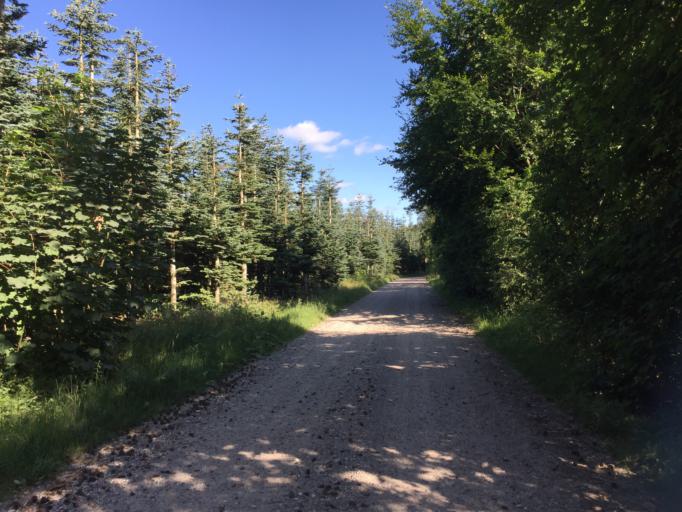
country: DK
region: South Denmark
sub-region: Kerteminde Kommune
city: Langeskov
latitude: 55.3609
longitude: 10.5516
